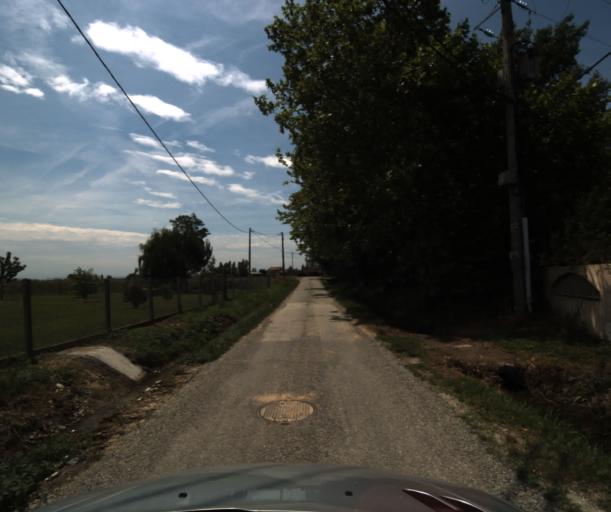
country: FR
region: Midi-Pyrenees
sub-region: Departement de la Haute-Garonne
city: Labastidette
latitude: 43.4501
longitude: 1.2413
